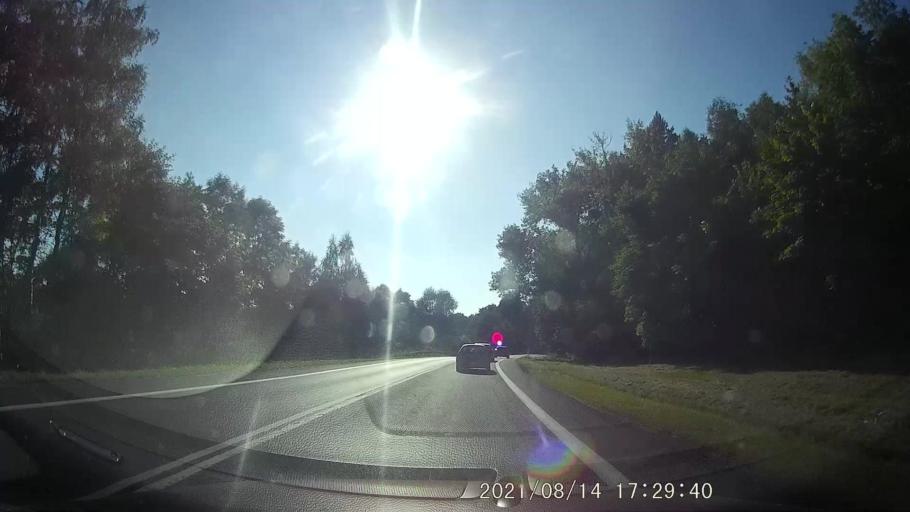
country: PL
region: Lower Silesian Voivodeship
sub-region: Jelenia Gora
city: Cieplice Slaskie Zdroj
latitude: 50.9103
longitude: 15.6664
